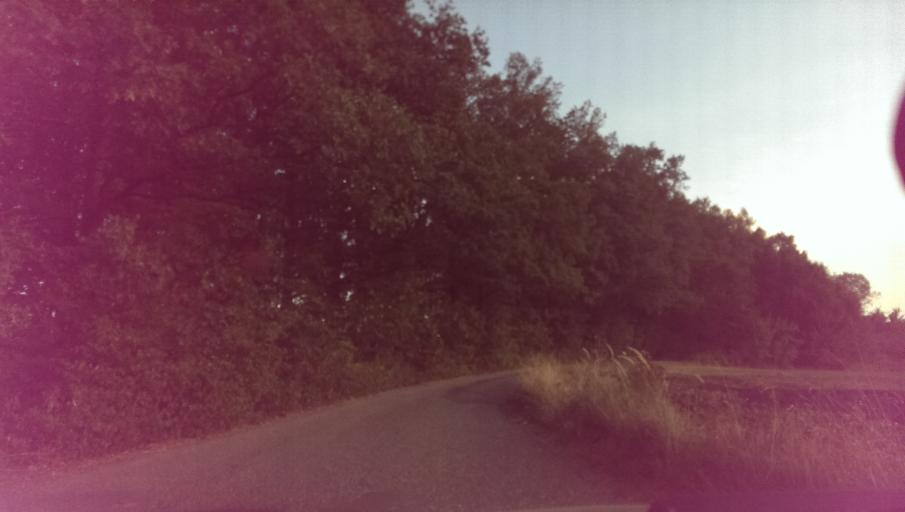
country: CZ
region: Zlin
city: Hvozdna
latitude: 49.2483
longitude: 17.7648
